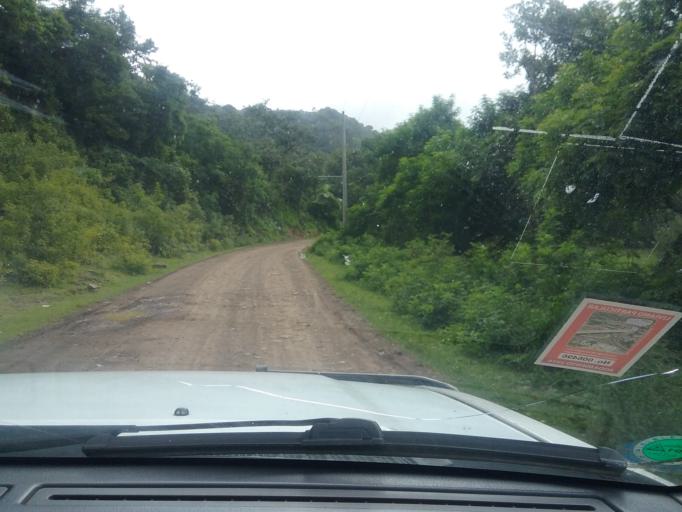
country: NI
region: Matagalpa
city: Matagalpa
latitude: 12.8723
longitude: -85.9488
